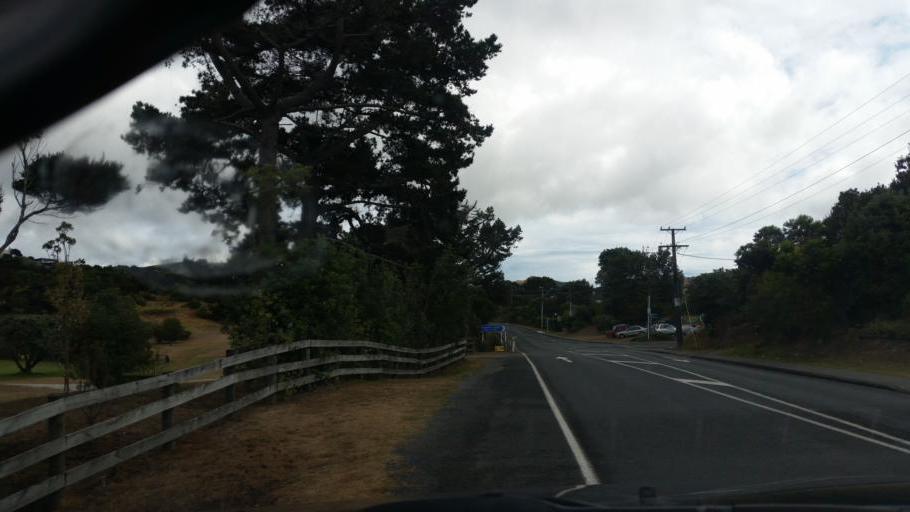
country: NZ
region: Auckland
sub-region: Auckland
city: Wellsford
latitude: -36.0963
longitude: 174.5862
